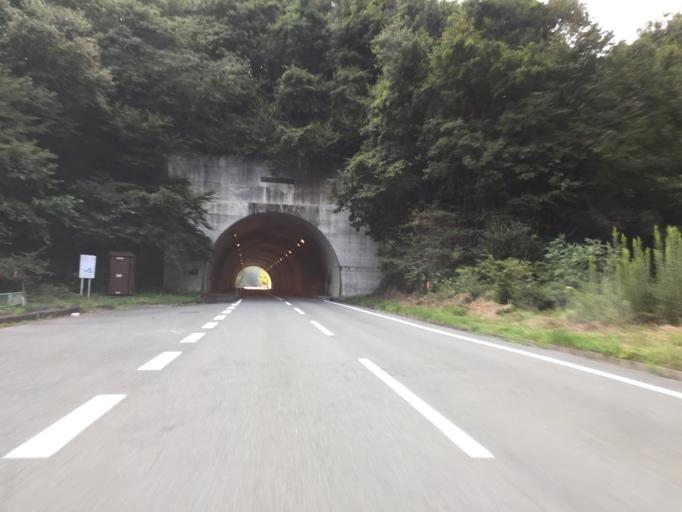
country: JP
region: Fukushima
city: Namie
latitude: 37.5244
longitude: 140.8861
